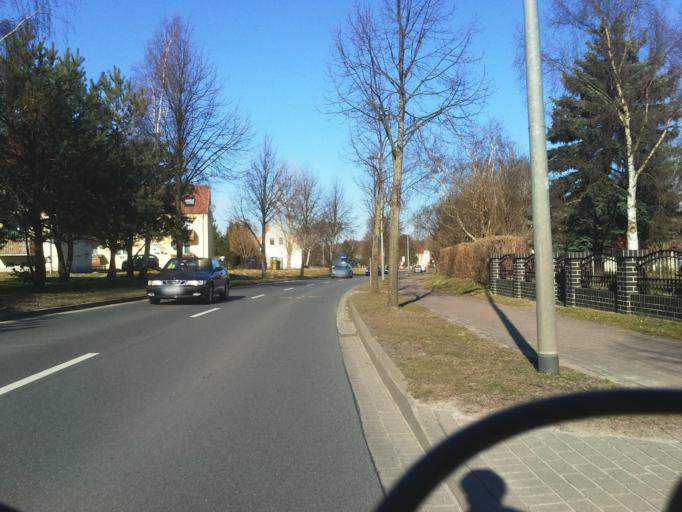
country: DE
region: Mecklenburg-Vorpommern
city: Nienhagen
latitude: 54.1469
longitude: 12.1699
